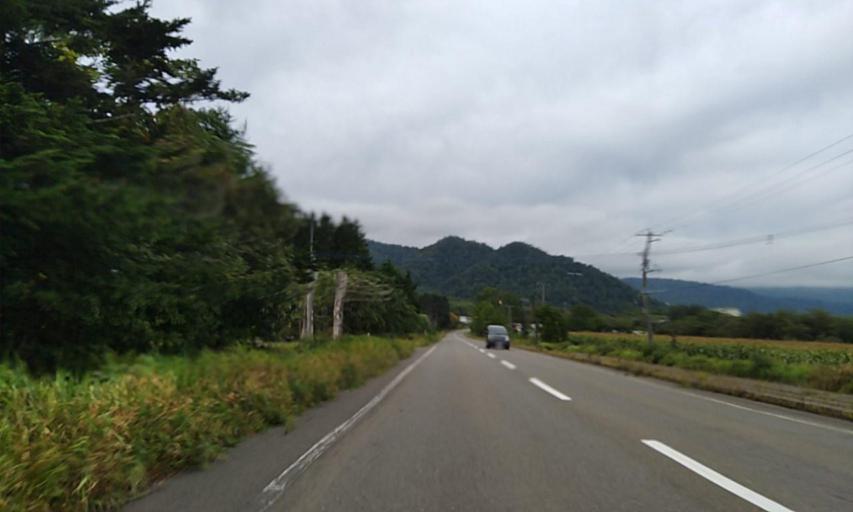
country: JP
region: Hokkaido
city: Bihoro
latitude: 43.5800
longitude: 144.2800
